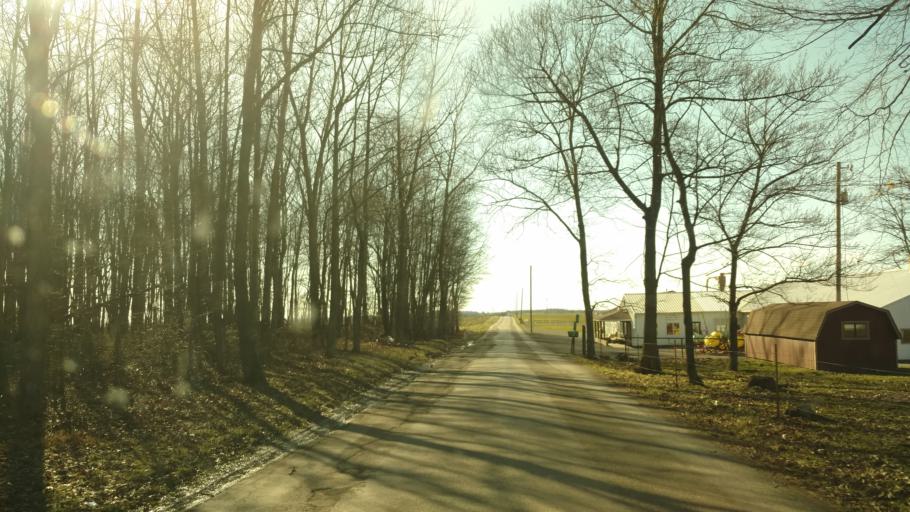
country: US
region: Ohio
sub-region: Wayne County
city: Apple Creek
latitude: 40.6460
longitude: -81.7793
